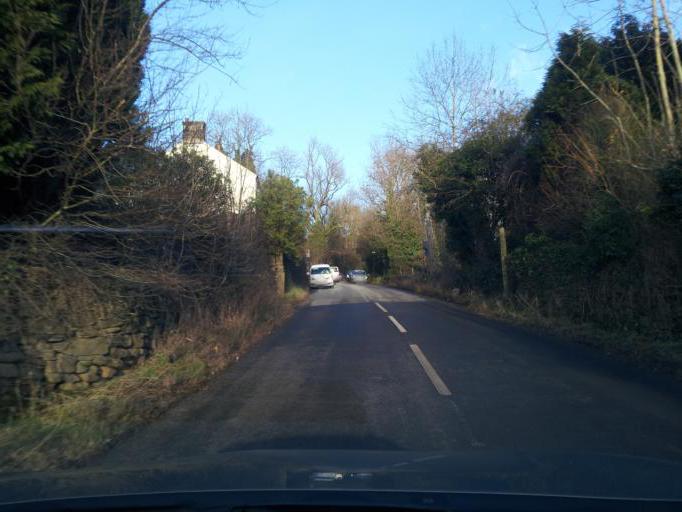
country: GB
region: England
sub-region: Derbyshire
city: Matlock
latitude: 53.1646
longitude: -1.5774
